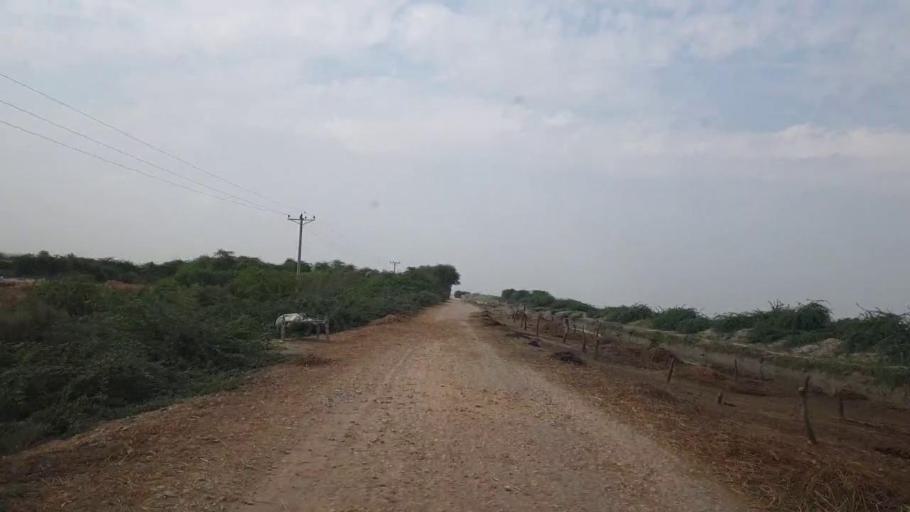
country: PK
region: Sindh
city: Kario
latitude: 24.6213
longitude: 68.5815
